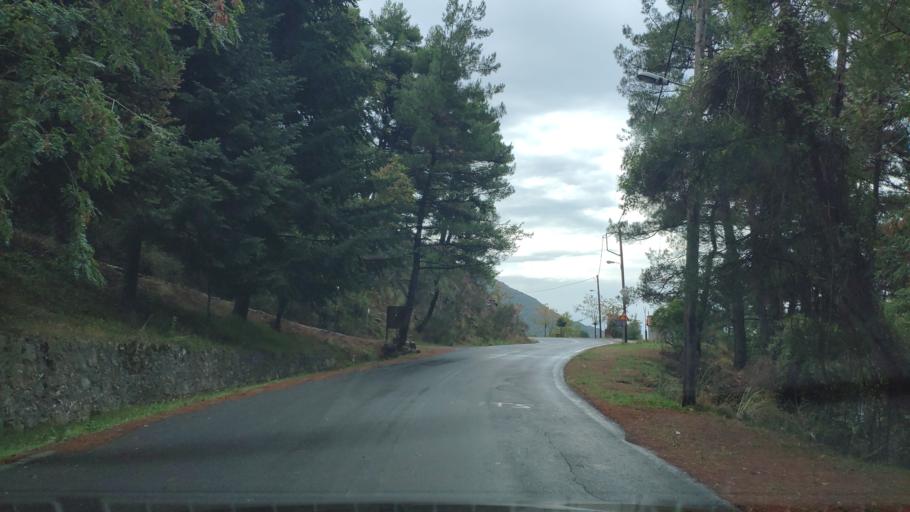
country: GR
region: Peloponnese
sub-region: Nomos Arkadias
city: Dimitsana
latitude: 37.5897
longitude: 22.0436
